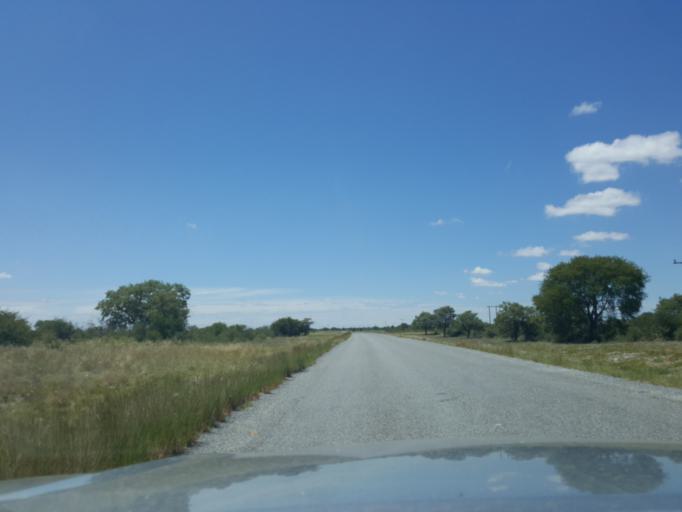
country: BW
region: Central
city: Nata
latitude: -20.1573
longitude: 25.8363
